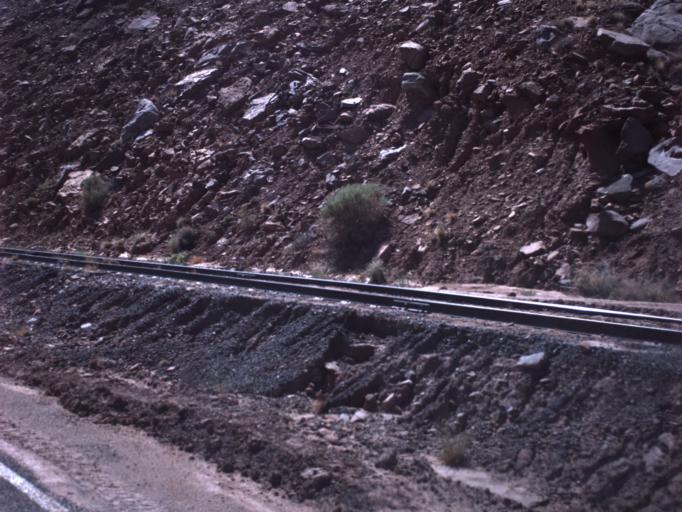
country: US
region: Utah
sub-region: Grand County
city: Moab
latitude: 38.5398
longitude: -109.6548
